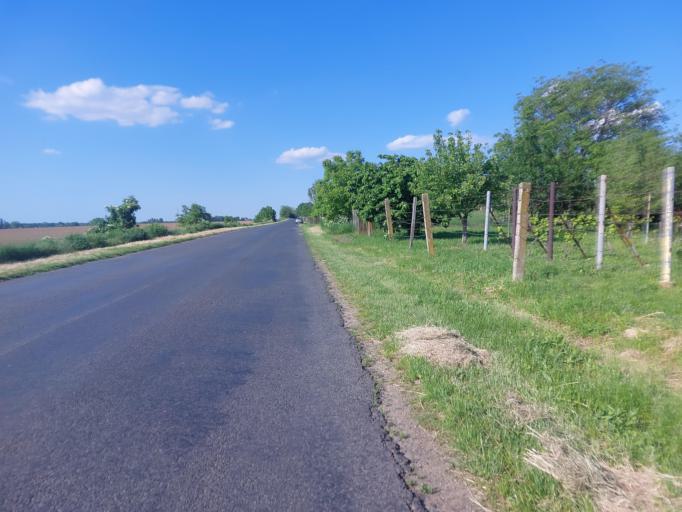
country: HU
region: Veszprem
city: Devecser
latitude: 47.1514
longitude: 17.3561
